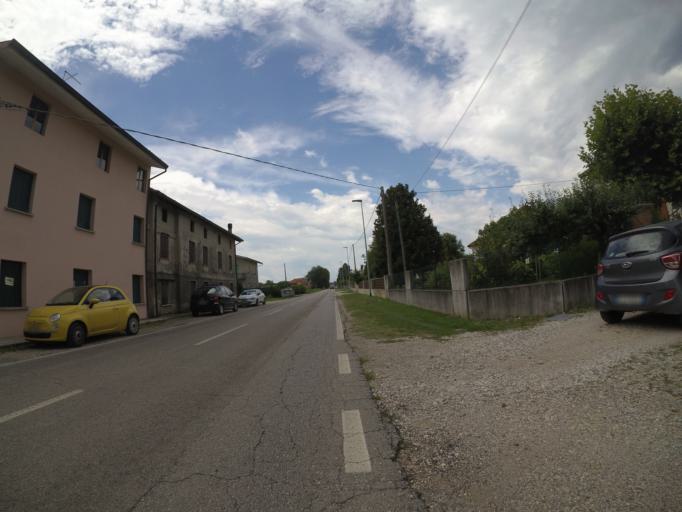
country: IT
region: Friuli Venezia Giulia
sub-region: Provincia di Udine
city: Talmassons
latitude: 45.9240
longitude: 13.1341
